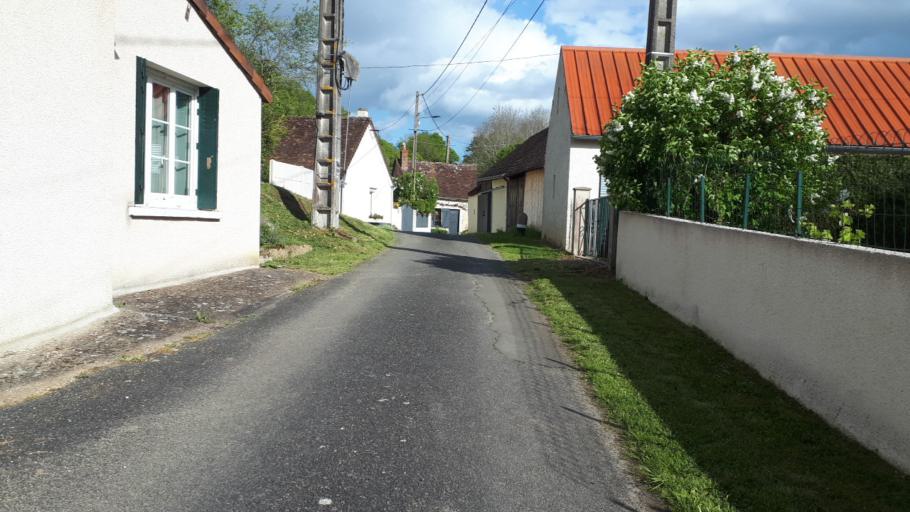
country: FR
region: Centre
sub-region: Departement du Loir-et-Cher
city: Aze
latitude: 47.8413
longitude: 0.9949
